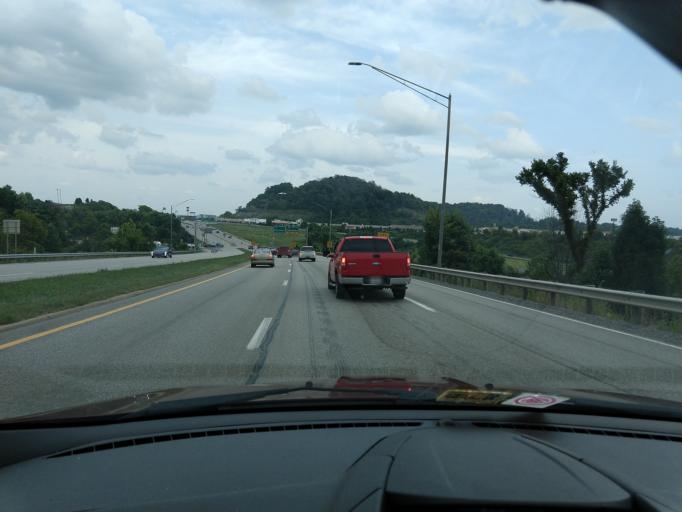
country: US
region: West Virginia
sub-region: Harrison County
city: Despard
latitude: 39.2777
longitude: -80.2882
